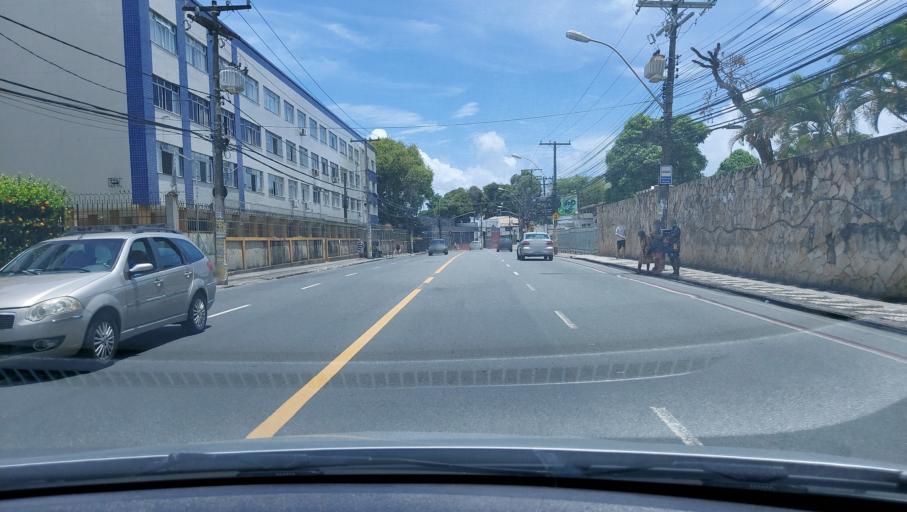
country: BR
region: Bahia
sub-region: Salvador
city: Salvador
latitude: -12.9899
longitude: -38.4901
